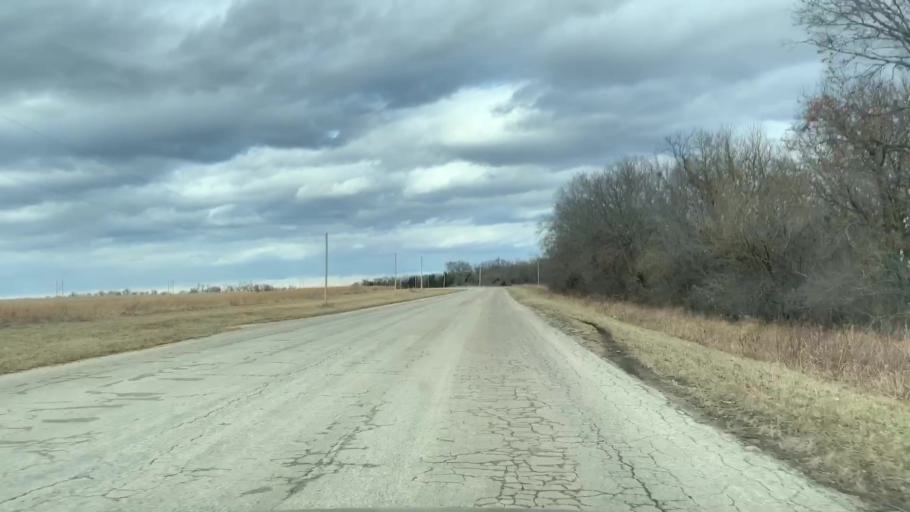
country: US
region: Kansas
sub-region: Allen County
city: Humboldt
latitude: 37.7588
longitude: -95.4715
